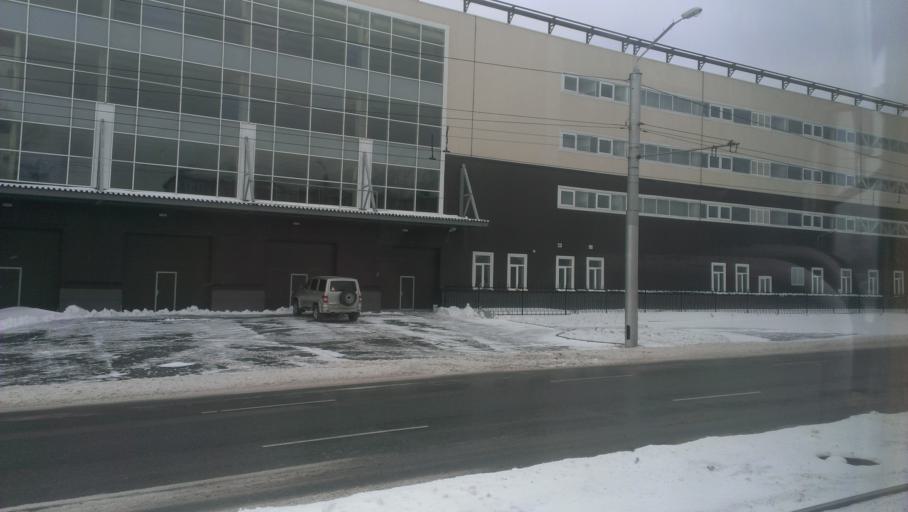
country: RU
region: Altai Krai
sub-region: Gorod Barnaulskiy
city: Barnaul
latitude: 53.3840
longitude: 83.7130
